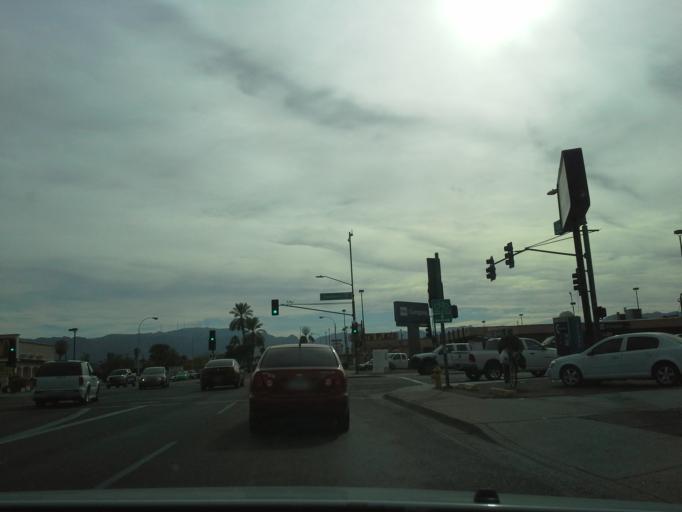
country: US
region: Arizona
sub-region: Maricopa County
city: Phoenix
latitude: 33.3926
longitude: -112.0734
